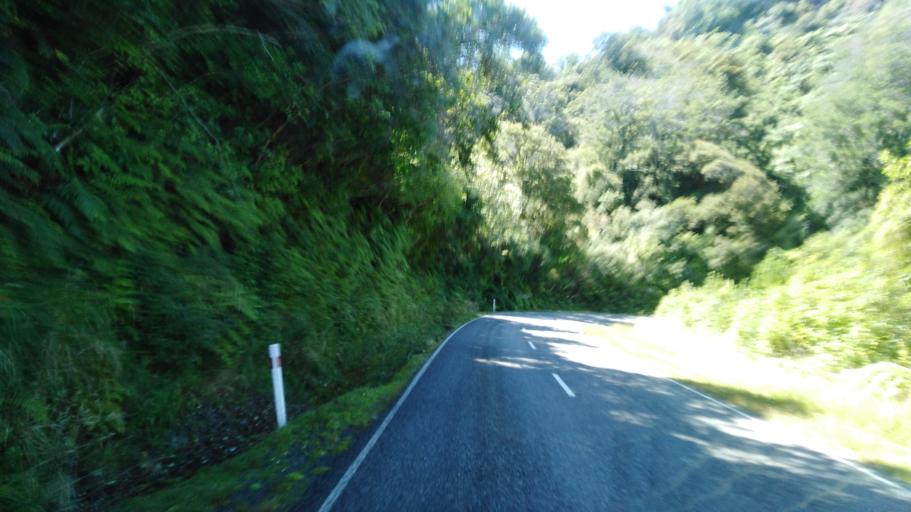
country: NZ
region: West Coast
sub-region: Buller District
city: Westport
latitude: -41.4895
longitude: 172.0491
